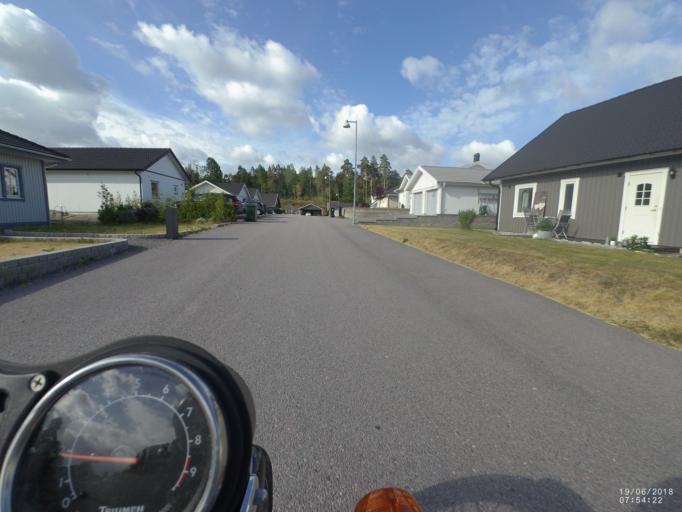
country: SE
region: Soedermanland
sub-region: Nykopings Kommun
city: Nykoping
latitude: 58.7784
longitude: 17.0121
